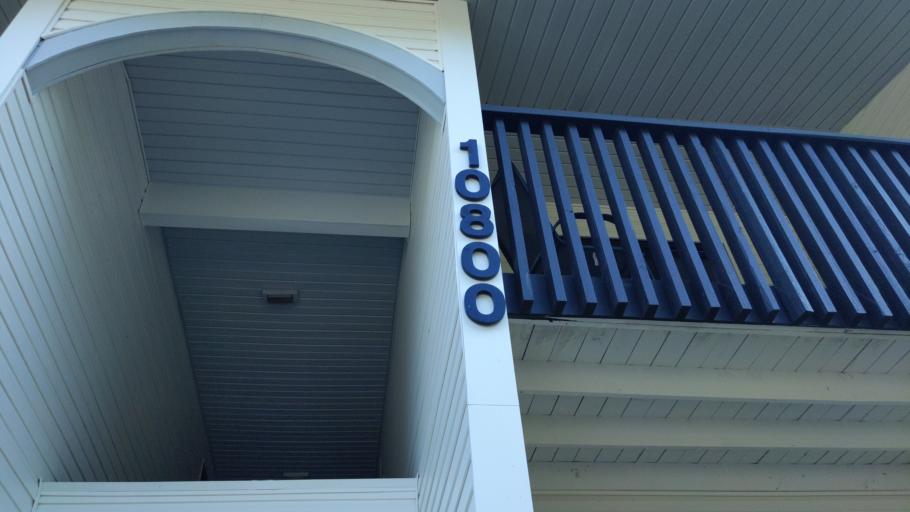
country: US
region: Virginia
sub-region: Montgomery County
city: Merrimac
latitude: 37.2147
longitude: -80.4462
